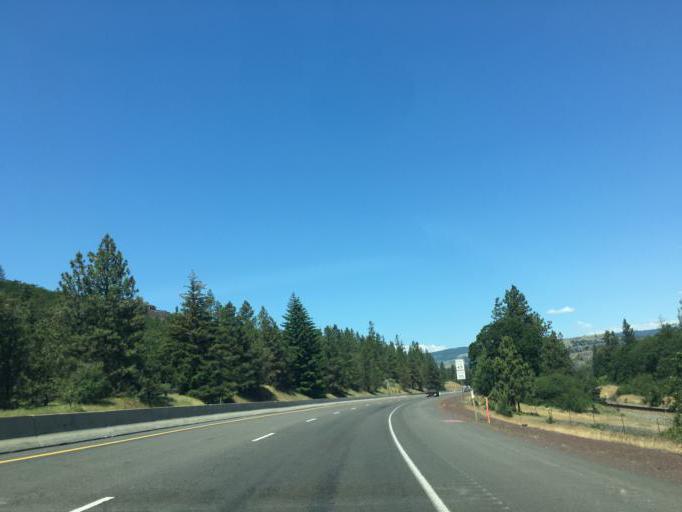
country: US
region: Oregon
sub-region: Wasco County
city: Chenoweth
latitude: 45.6781
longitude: -121.2881
